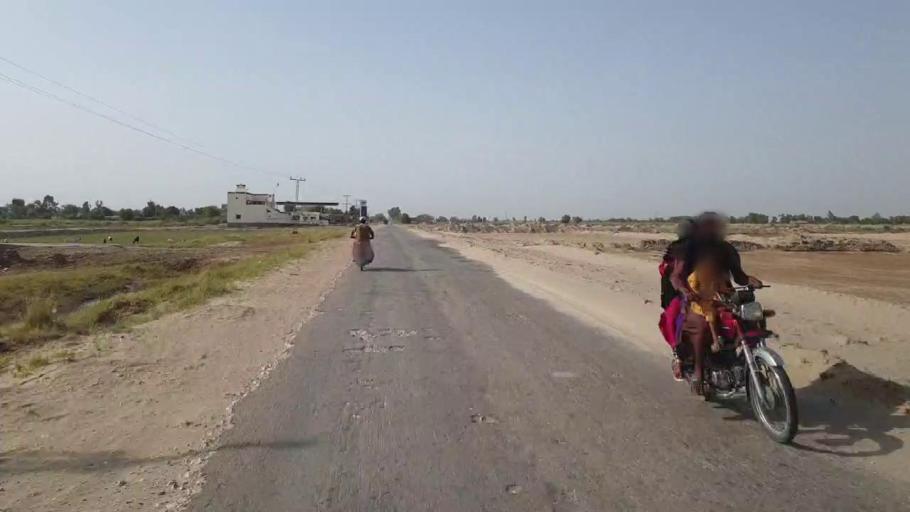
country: PK
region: Sindh
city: Sanghar
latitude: 26.2839
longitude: 68.9306
